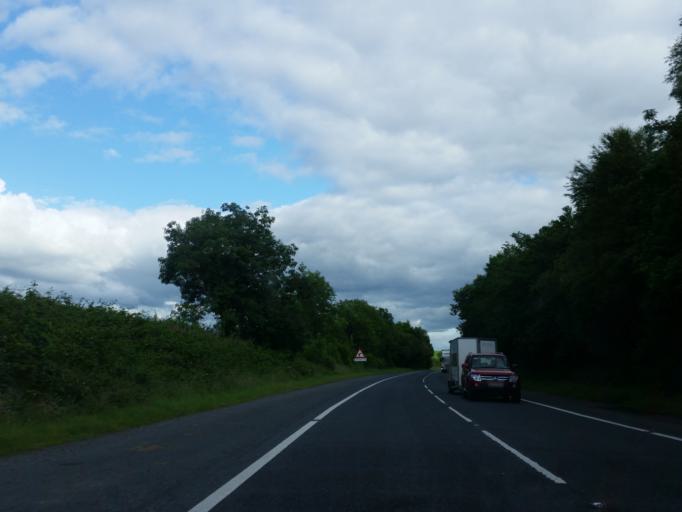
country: GB
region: Northern Ireland
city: Lisnaskea
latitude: 54.3111
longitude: -7.4975
